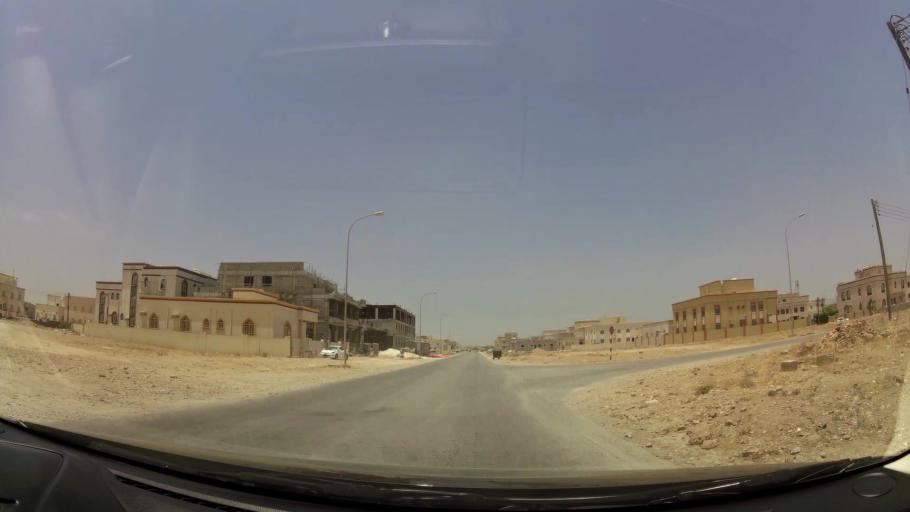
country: OM
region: Zufar
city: Salalah
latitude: 17.0913
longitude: 54.1565
